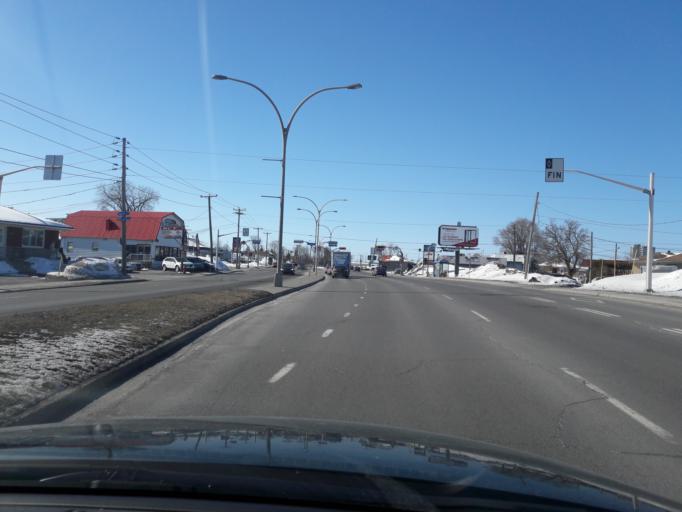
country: CA
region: Quebec
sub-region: Laurentides
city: Rosemere
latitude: 45.5606
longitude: -73.7709
